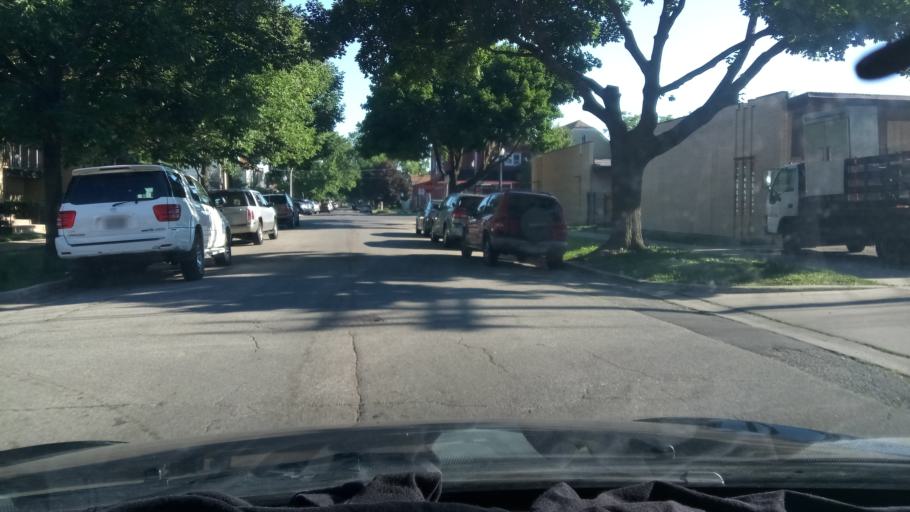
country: US
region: Illinois
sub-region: Cook County
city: Hometown
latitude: 41.7776
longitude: -87.7312
